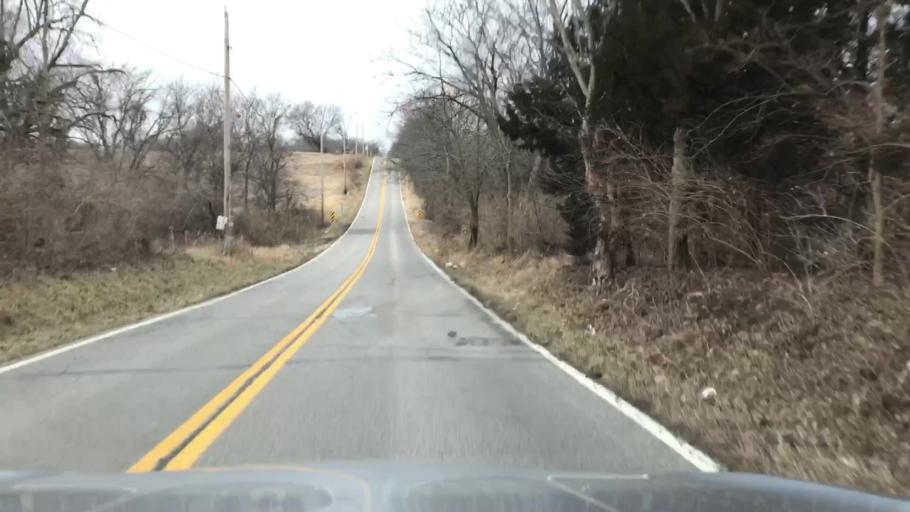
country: US
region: Missouri
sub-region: Jackson County
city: Lees Summit
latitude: 38.8897
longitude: -94.4032
